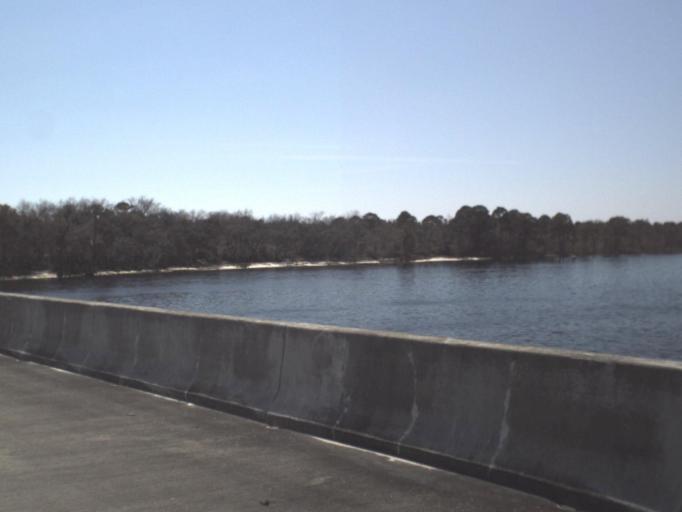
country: US
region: Florida
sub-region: Wakulla County
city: Crawfordville
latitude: 29.9629
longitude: -84.3845
